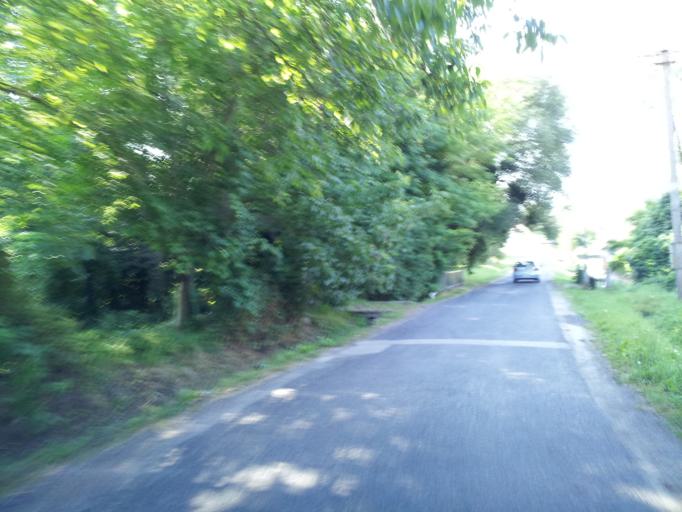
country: HU
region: Zala
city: Cserszegtomaj
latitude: 46.8900
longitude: 17.2268
